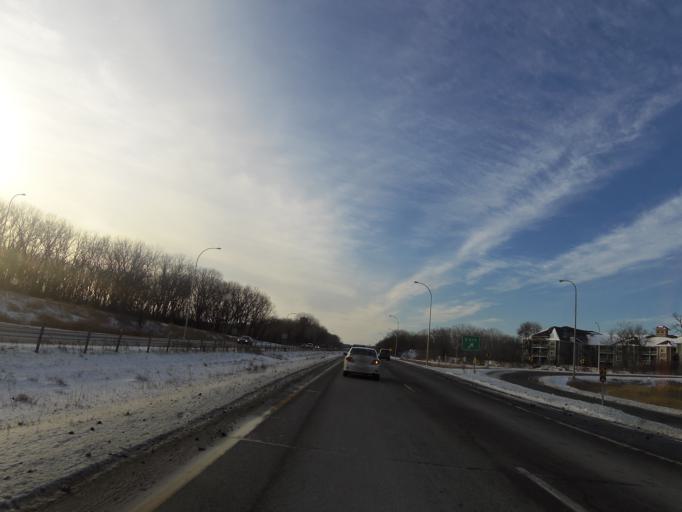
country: US
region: Minnesota
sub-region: Hennepin County
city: Edina
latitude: 44.8875
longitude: -93.3696
